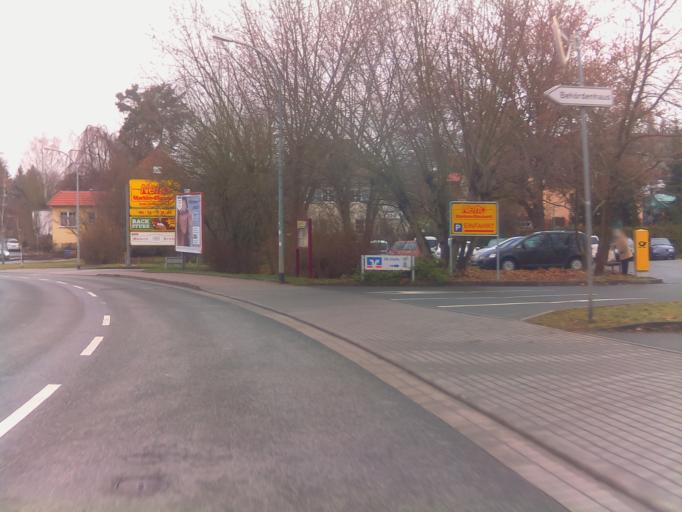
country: DE
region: Thuringia
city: Stadtroda
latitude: 50.8626
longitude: 11.7361
